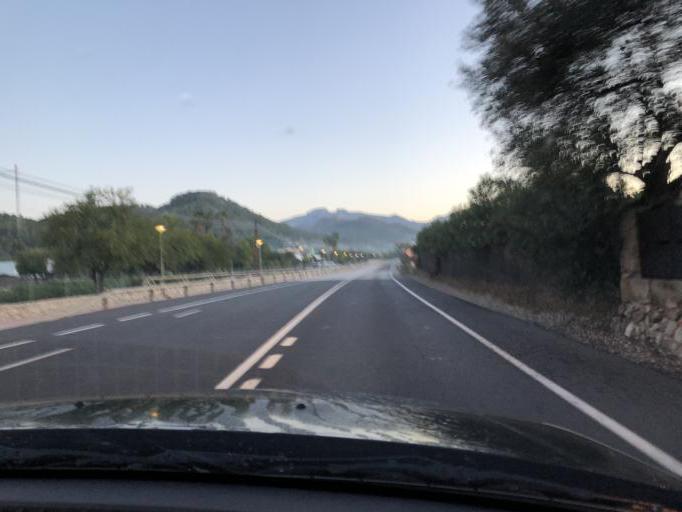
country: ES
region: Balearic Islands
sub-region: Illes Balears
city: Andratx
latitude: 39.5609
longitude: 2.4013
